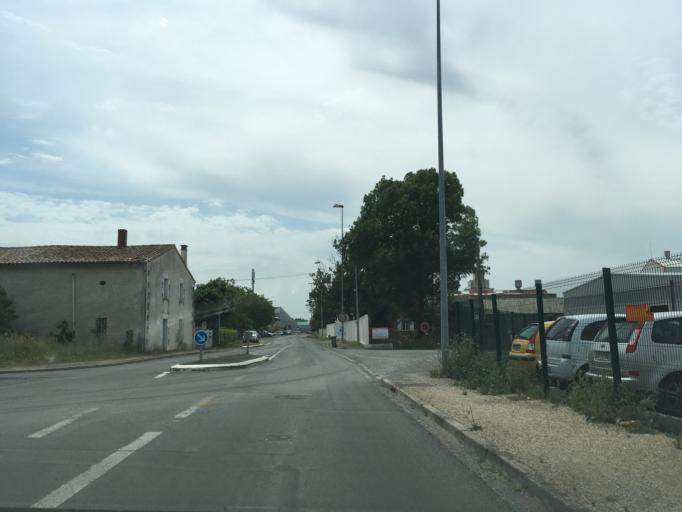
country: FR
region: Poitou-Charentes
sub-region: Departement des Deux-Sevres
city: Niort
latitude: 46.3075
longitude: -0.4607
